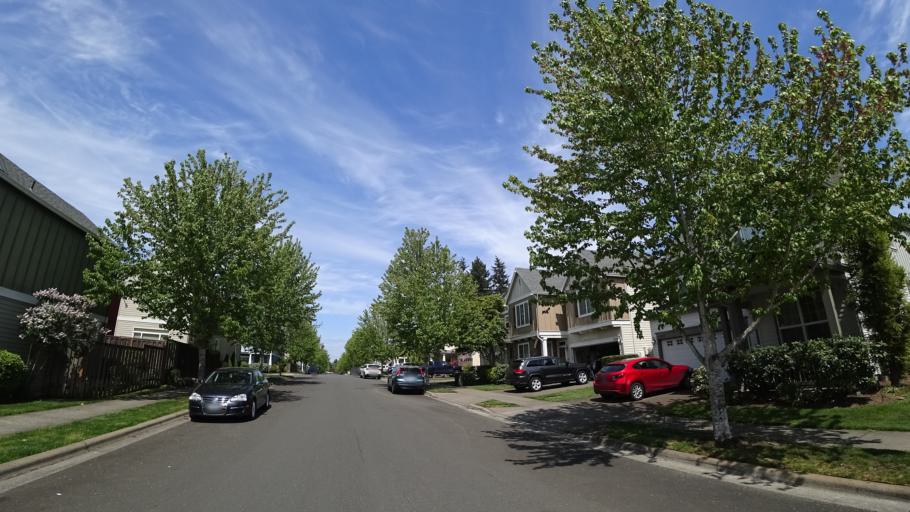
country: US
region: Oregon
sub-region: Washington County
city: Aloha
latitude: 45.4739
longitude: -122.8885
